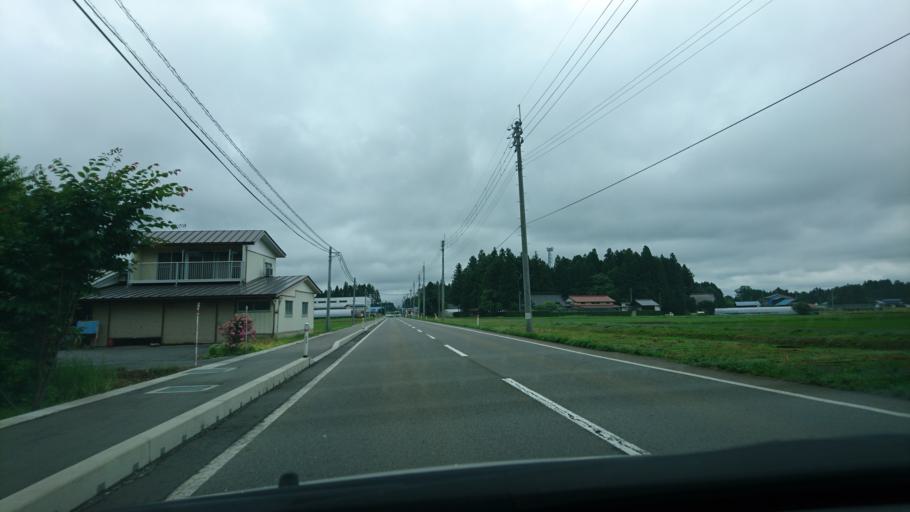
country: JP
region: Iwate
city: Mizusawa
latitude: 39.1045
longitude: 141.0517
